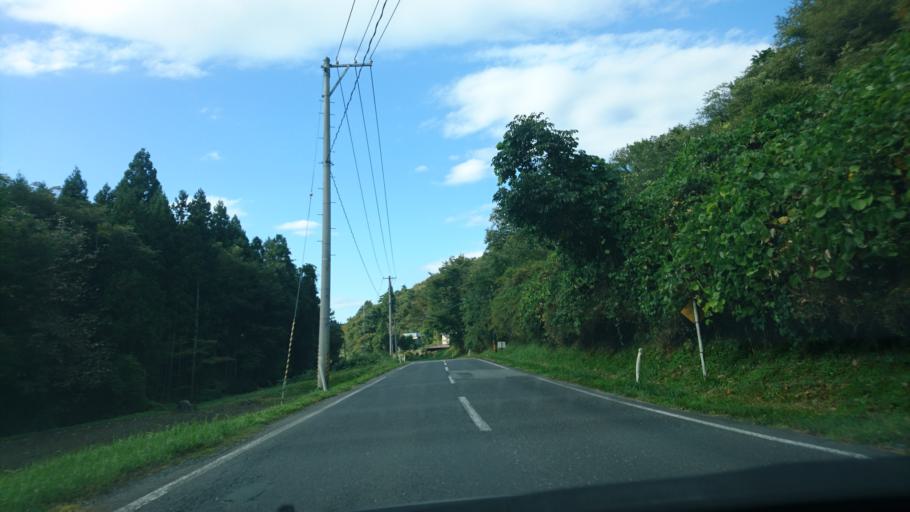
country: JP
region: Iwate
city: Ichinoseki
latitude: 38.8728
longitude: 141.3445
